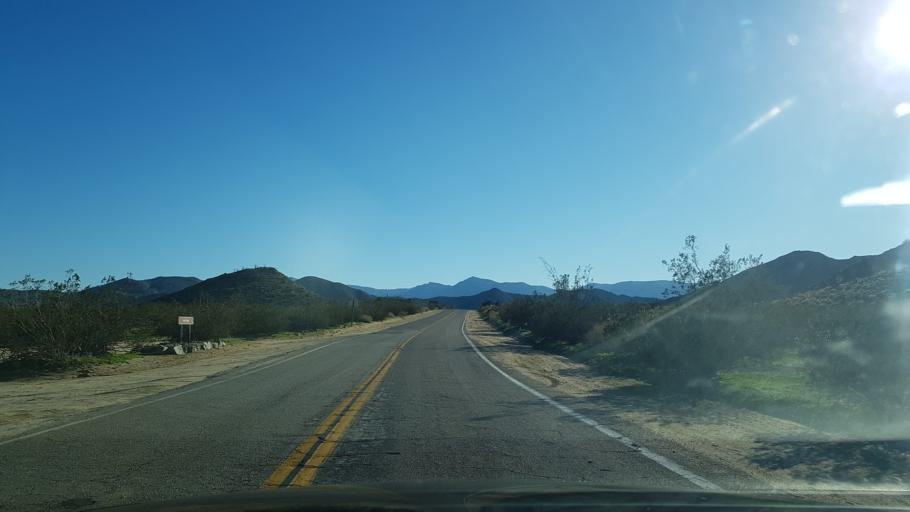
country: US
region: California
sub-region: San Diego County
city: Julian
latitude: 33.0376
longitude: -116.4106
